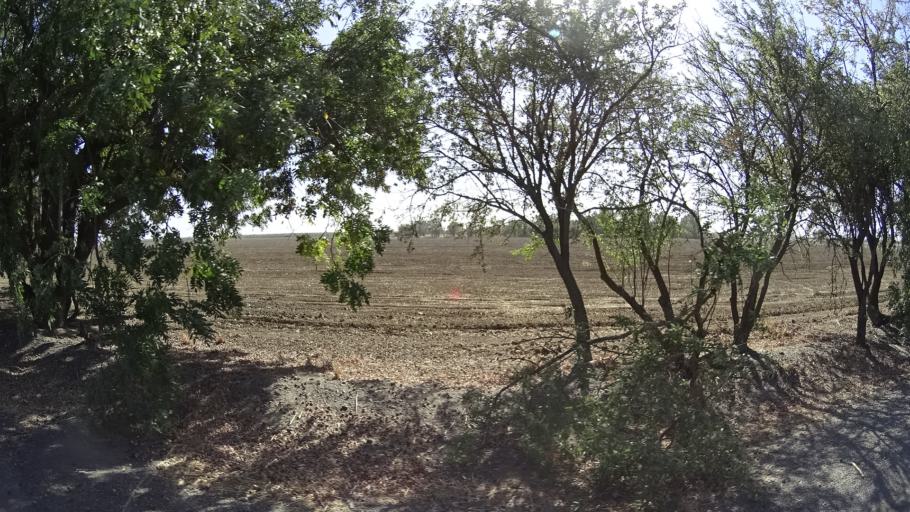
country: US
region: California
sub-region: Yolo County
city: Davis
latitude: 38.5904
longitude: -121.7953
